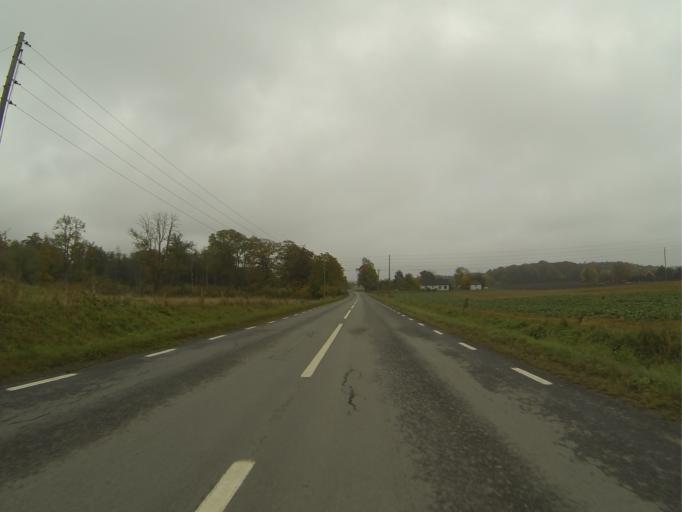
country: SE
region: Skane
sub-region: Tomelilla Kommun
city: Tomelilla
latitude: 55.6087
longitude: 13.9293
